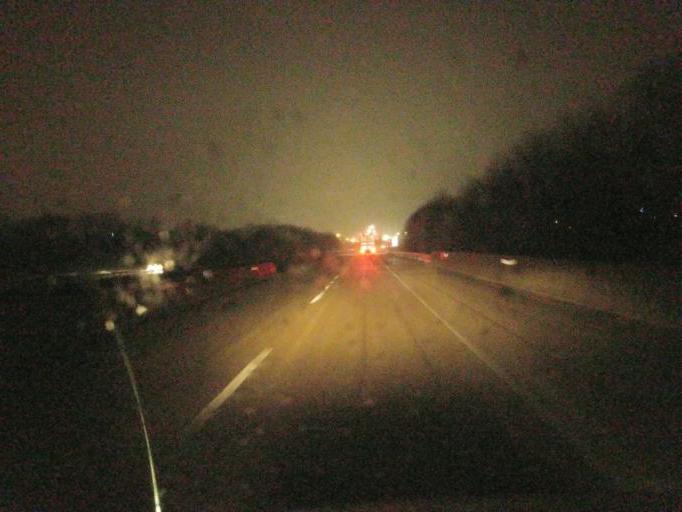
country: US
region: Illinois
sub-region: Fayette County
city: Vandalia
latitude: 38.9771
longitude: -89.0872
